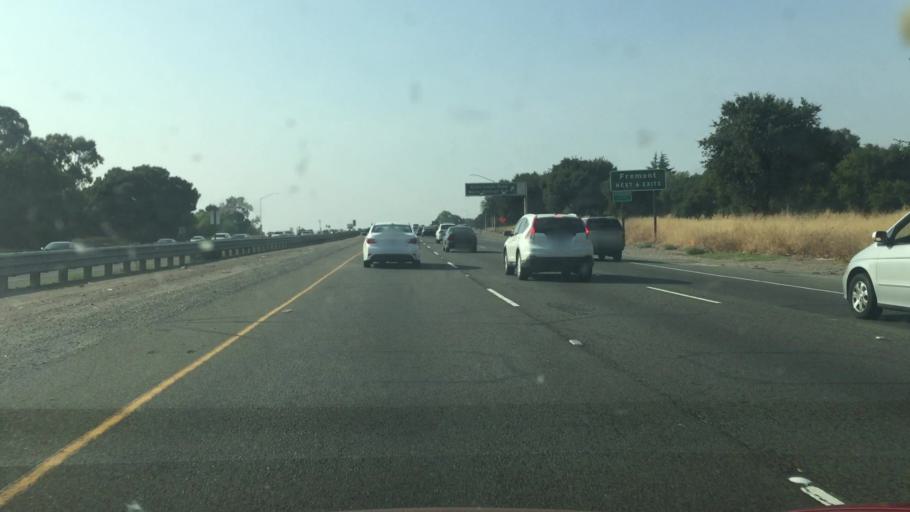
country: US
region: California
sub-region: Santa Clara County
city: Milpitas
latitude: 37.4616
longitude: -121.9017
